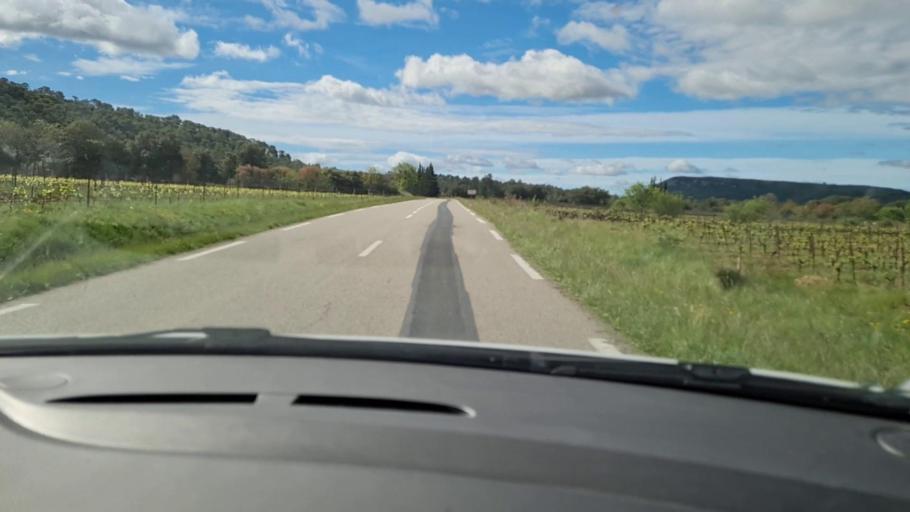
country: FR
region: Languedoc-Roussillon
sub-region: Departement du Gard
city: Quissac
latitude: 43.8498
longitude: 4.0187
